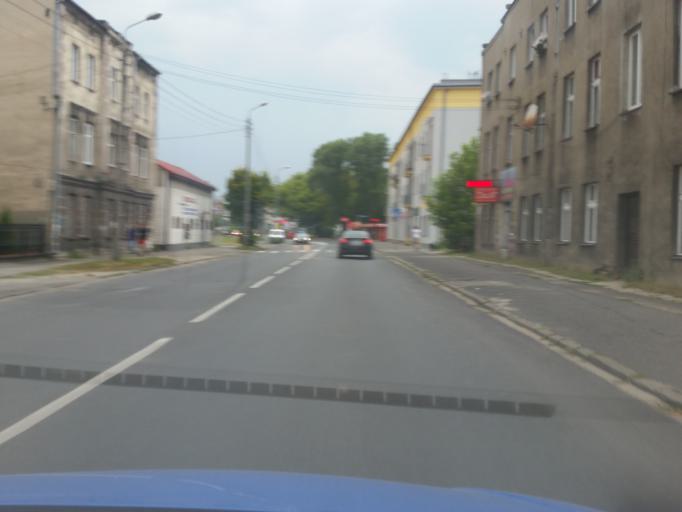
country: PL
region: Silesian Voivodeship
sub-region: Sosnowiec
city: Sosnowiec
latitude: 50.2877
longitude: 19.1189
